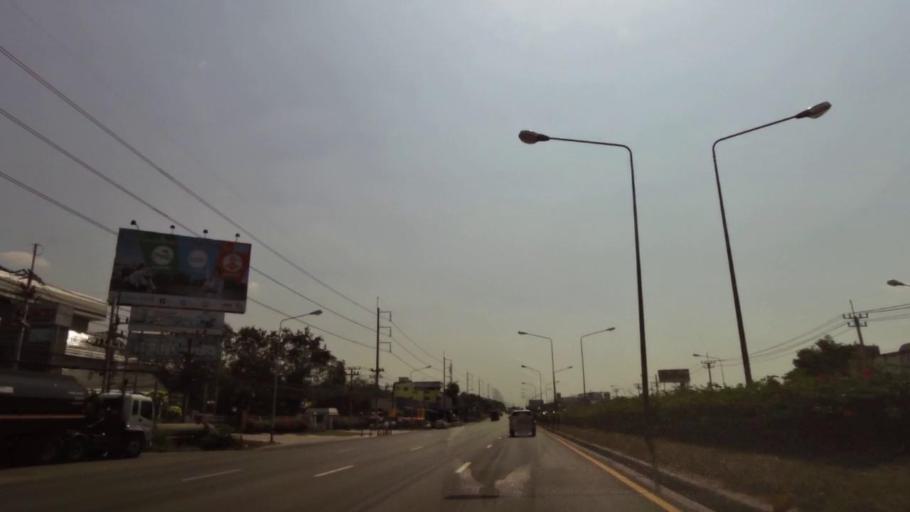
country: TH
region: Chon Buri
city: Chon Buri
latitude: 13.3713
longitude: 101.0191
